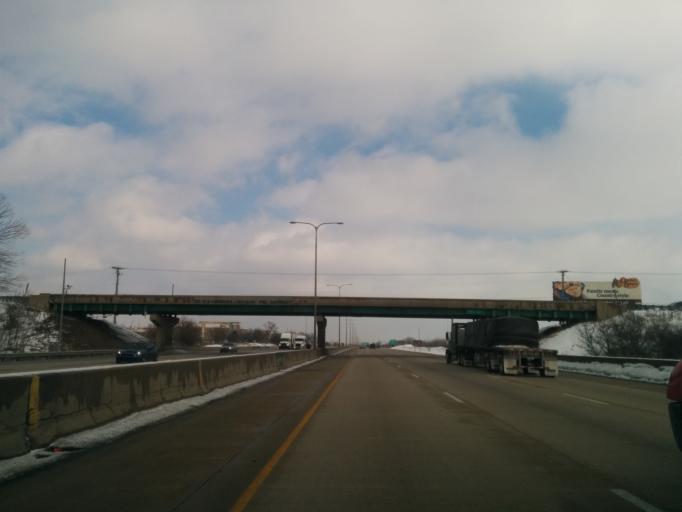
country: US
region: Illinois
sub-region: Will County
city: Frankfort Square
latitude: 41.5507
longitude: -87.8132
